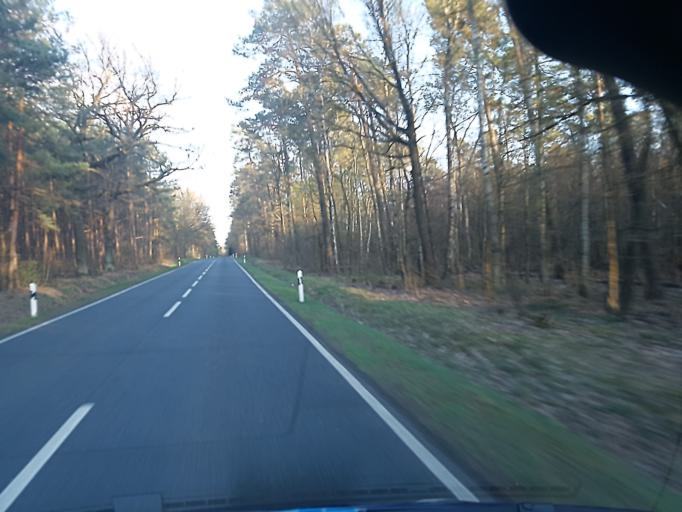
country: DE
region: Saxony
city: Kossa
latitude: 51.5749
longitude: 12.7420
